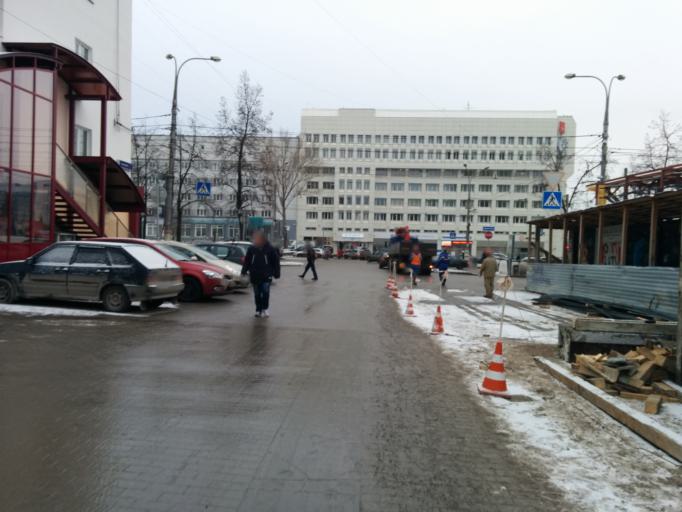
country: RU
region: Perm
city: Perm
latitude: 58.0106
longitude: 56.2403
